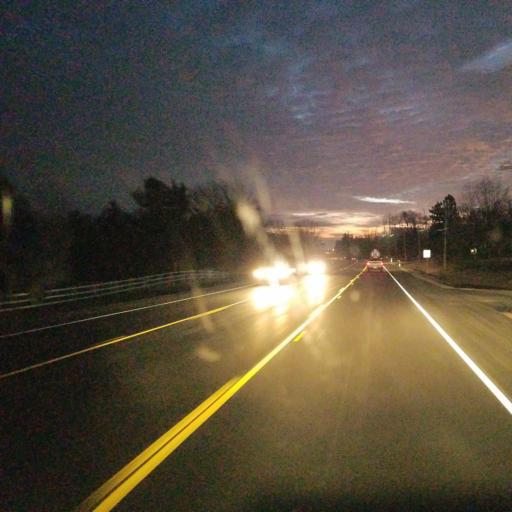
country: US
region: Illinois
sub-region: Peoria County
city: Hanna City
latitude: 40.6920
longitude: -89.7725
